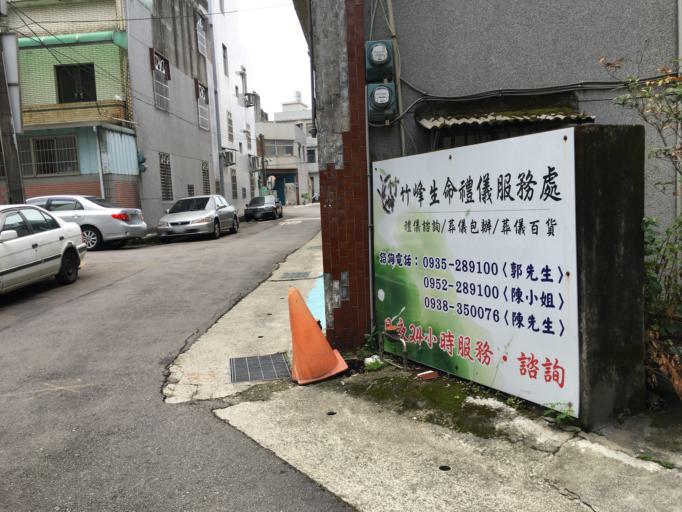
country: TW
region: Taiwan
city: Taoyuan City
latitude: 24.9487
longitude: 121.2472
